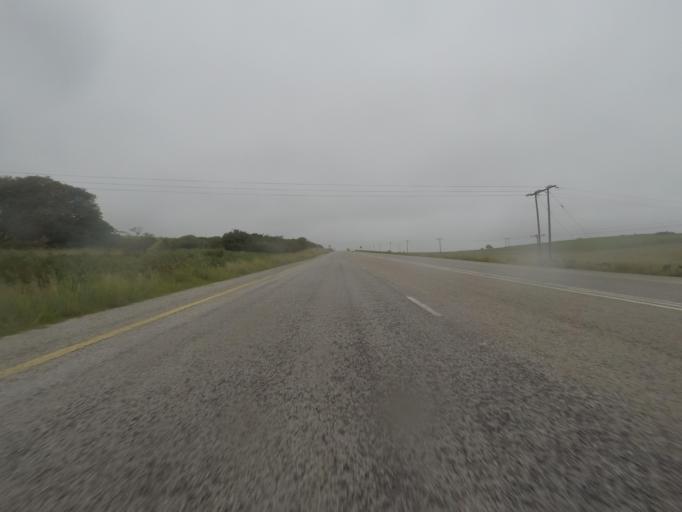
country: ZA
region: Eastern Cape
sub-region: Cacadu District Municipality
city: Grahamstown
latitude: -33.6239
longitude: 26.2949
